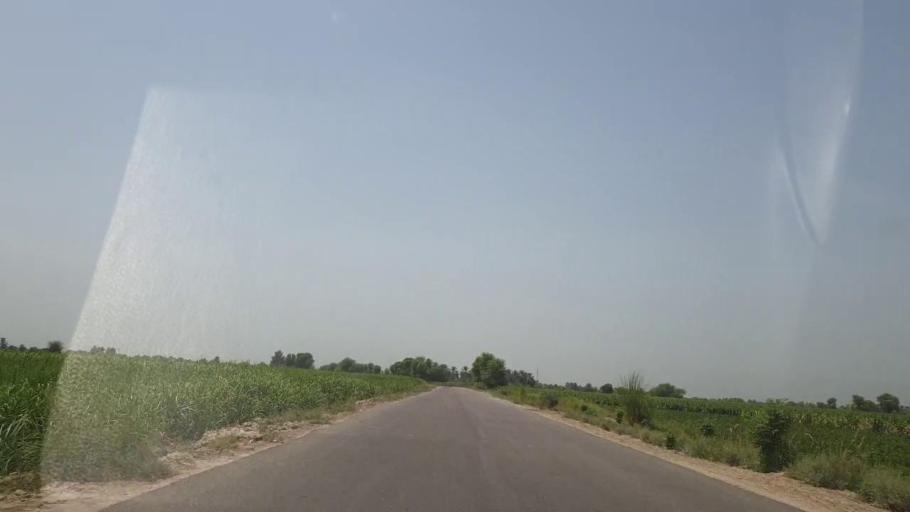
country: PK
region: Sindh
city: Ranipur
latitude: 27.2949
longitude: 68.6047
